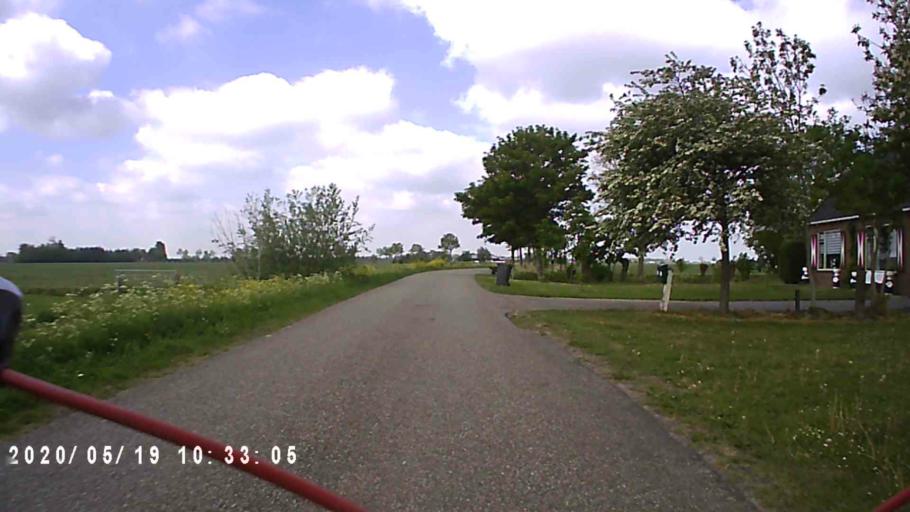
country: NL
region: Friesland
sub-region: Gemeente Kollumerland en Nieuwkruisland
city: Kollum
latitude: 53.2881
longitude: 6.1908
